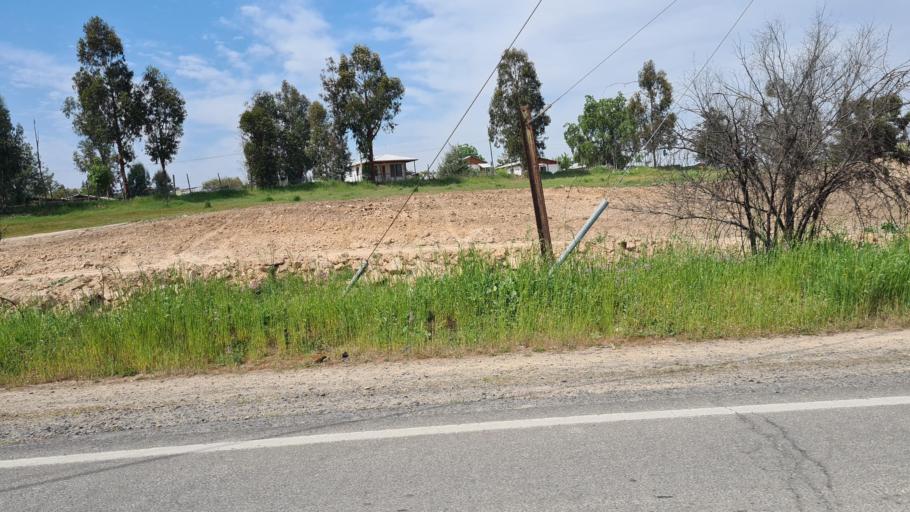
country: CL
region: O'Higgins
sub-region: Provincia de Cachapoal
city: San Vicente
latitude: -34.1607
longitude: -71.4275
